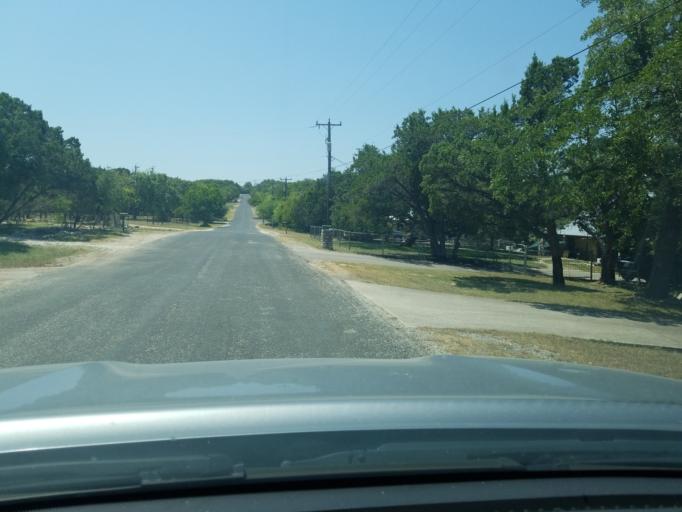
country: US
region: Texas
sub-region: Bexar County
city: Timberwood Park
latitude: 29.7135
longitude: -98.4924
